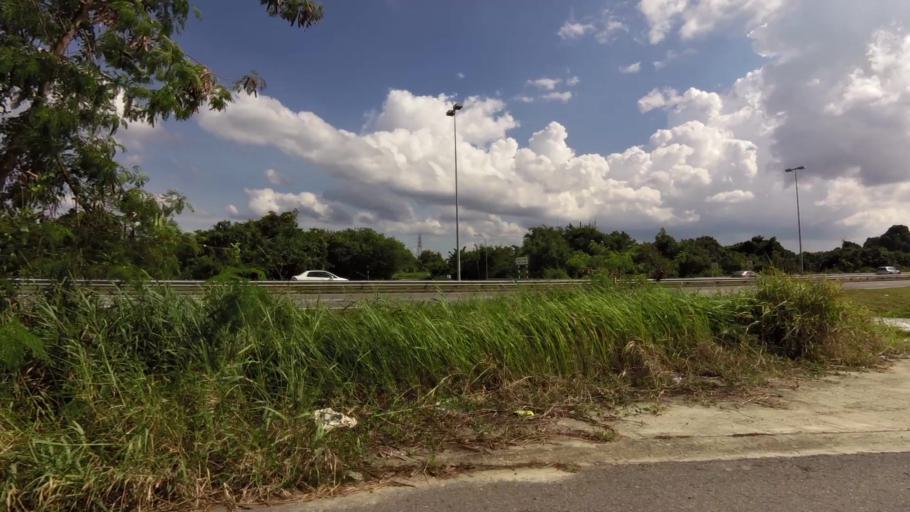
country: BN
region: Brunei and Muara
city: Bandar Seri Begawan
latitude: 4.9518
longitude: 114.9507
